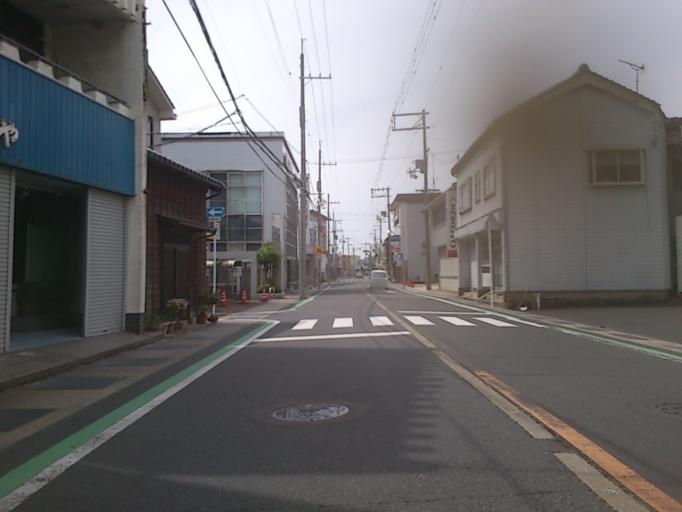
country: JP
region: Kyoto
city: Miyazu
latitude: 35.6813
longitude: 135.0281
